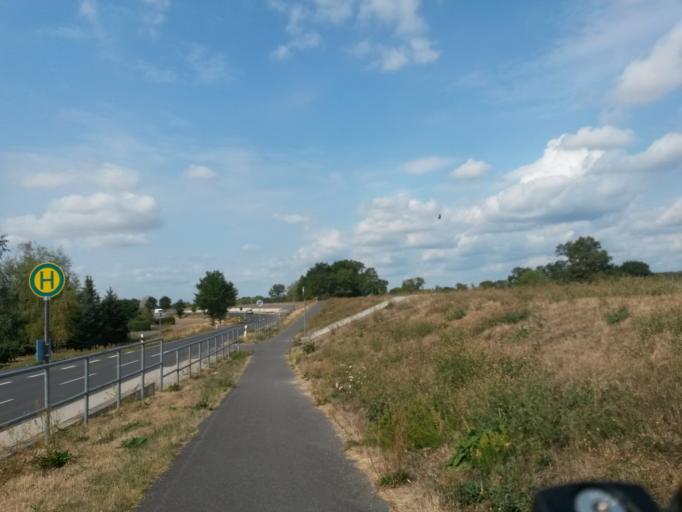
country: DE
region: Saxony-Anhalt
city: Abtsdorf
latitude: 51.8413
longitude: 12.6887
